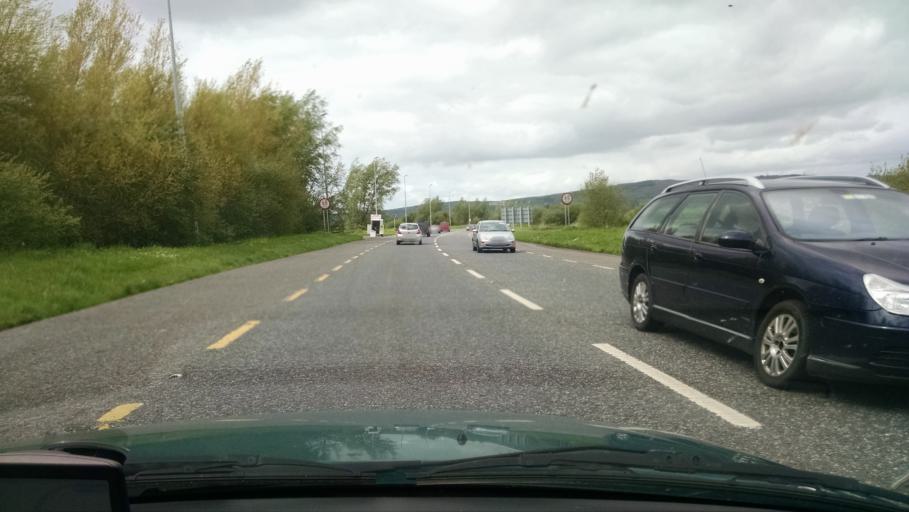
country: IE
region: Munster
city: Moyross
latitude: 52.6661
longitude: -8.6712
